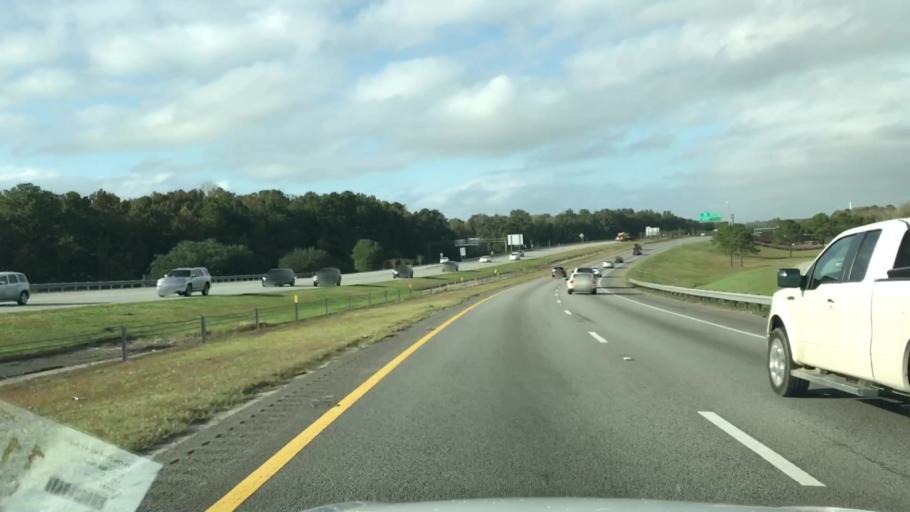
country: US
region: South Carolina
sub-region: Charleston County
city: North Charleston
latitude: 32.8651
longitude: -80.0268
